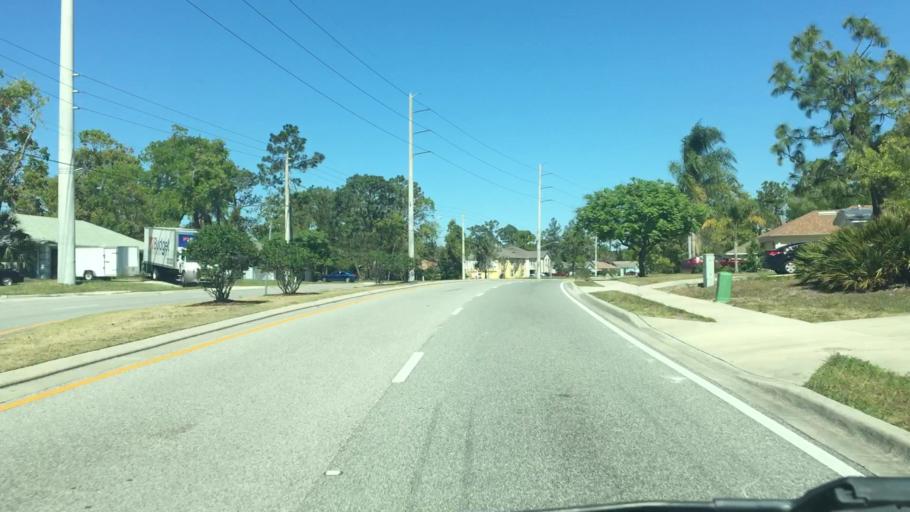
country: US
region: Florida
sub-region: Volusia County
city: Deltona
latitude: 28.9095
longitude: -81.1803
